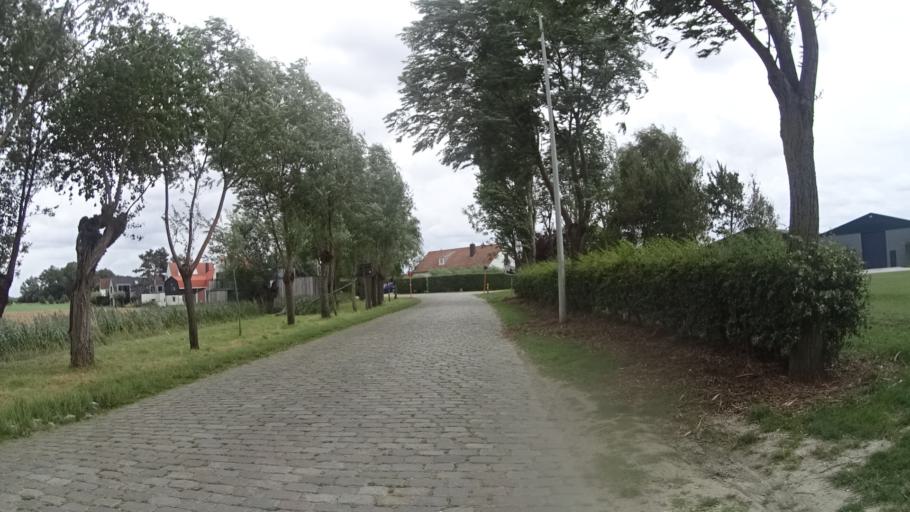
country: BE
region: Flanders
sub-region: Provincie West-Vlaanderen
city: Knokke-Heist
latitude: 51.3375
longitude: 3.3254
